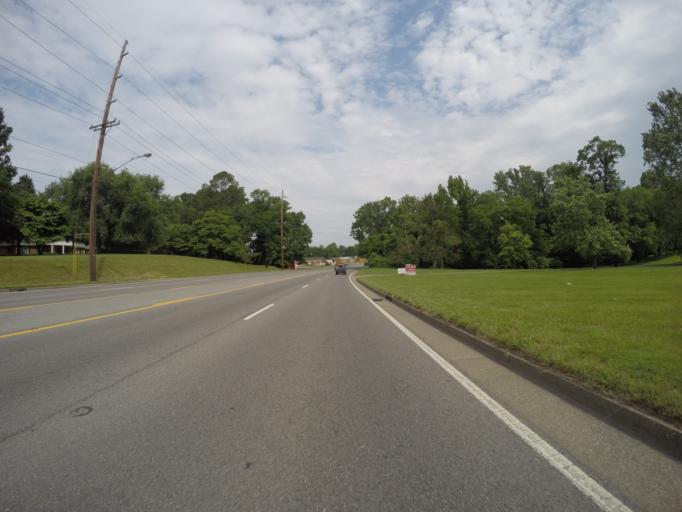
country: US
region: Tennessee
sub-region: Davidson County
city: Lakewood
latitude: 36.2600
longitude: -86.6596
